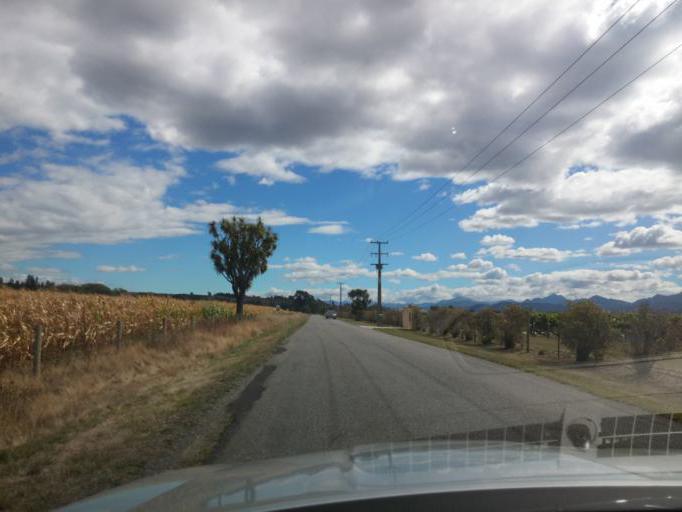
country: NZ
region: Marlborough
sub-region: Marlborough District
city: Blenheim
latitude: -41.5265
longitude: 173.8346
